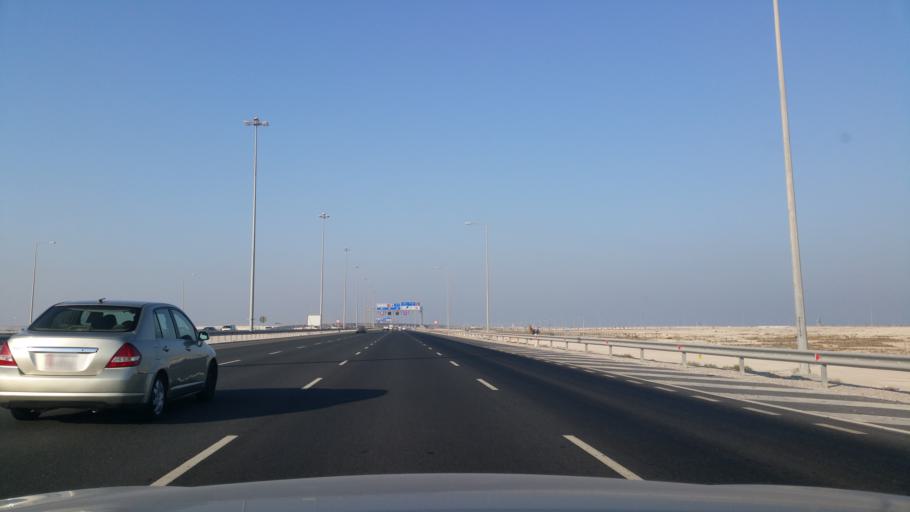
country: QA
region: Al Wakrah
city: Al Wukayr
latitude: 25.1101
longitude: 51.5837
